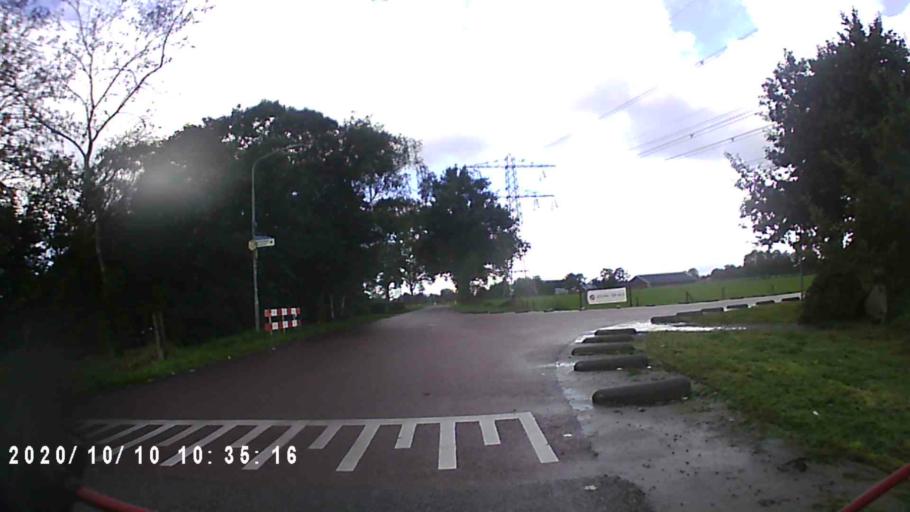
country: NL
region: Groningen
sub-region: Gemeente Grootegast
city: Grootegast
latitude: 53.1892
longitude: 6.3103
